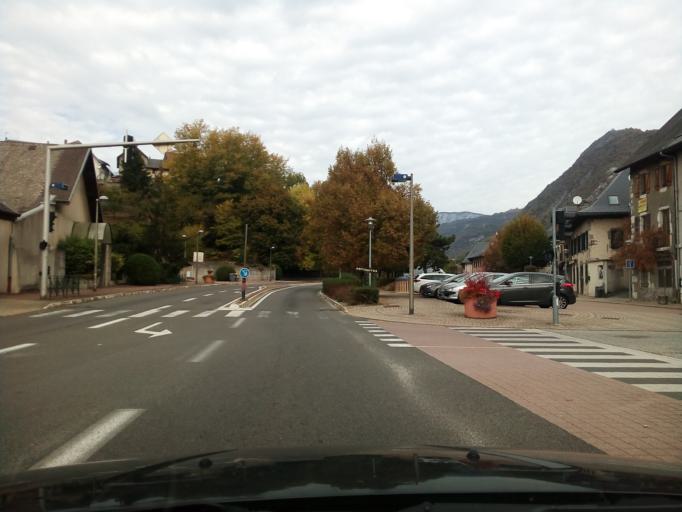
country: FR
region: Rhone-Alpes
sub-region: Departement de la Savoie
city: Challes-les-Eaux
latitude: 45.5328
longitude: 5.9922
